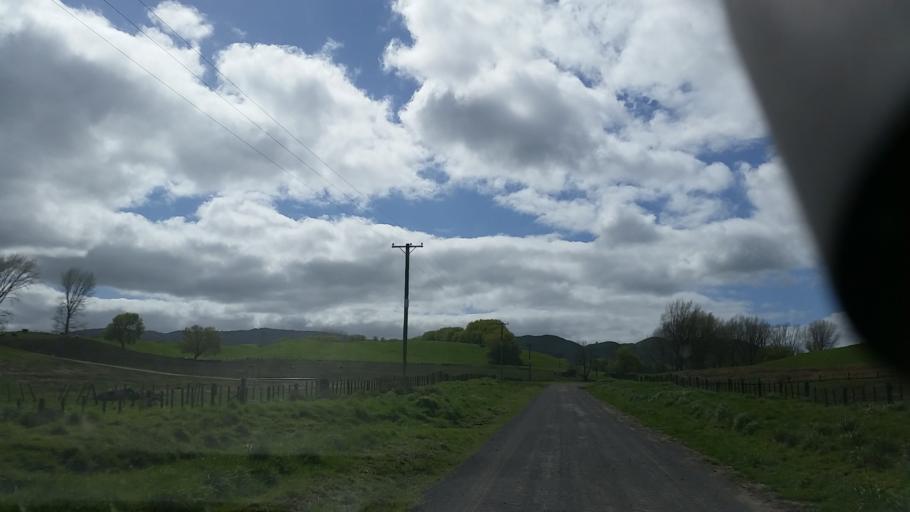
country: NZ
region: Bay of Plenty
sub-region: Rotorua District
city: Rotorua
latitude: -38.3193
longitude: 176.2987
